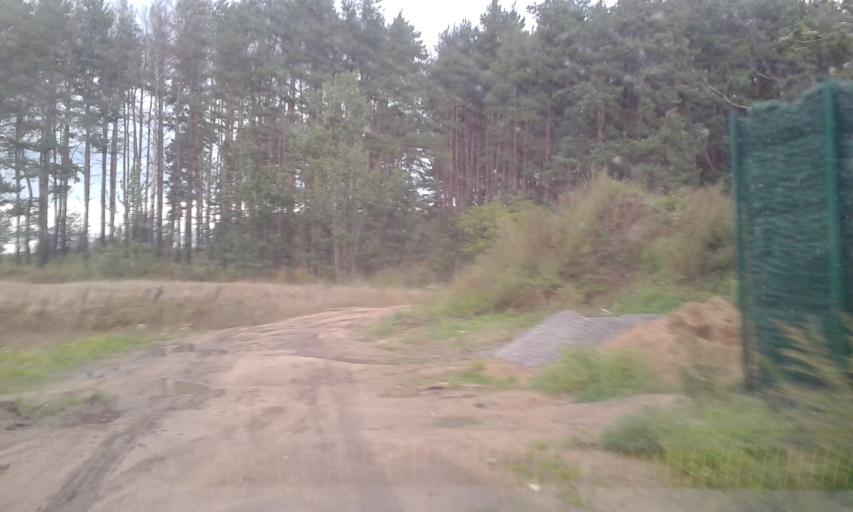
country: BY
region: Minsk
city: Bal'shavik
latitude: 53.9521
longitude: 27.5688
